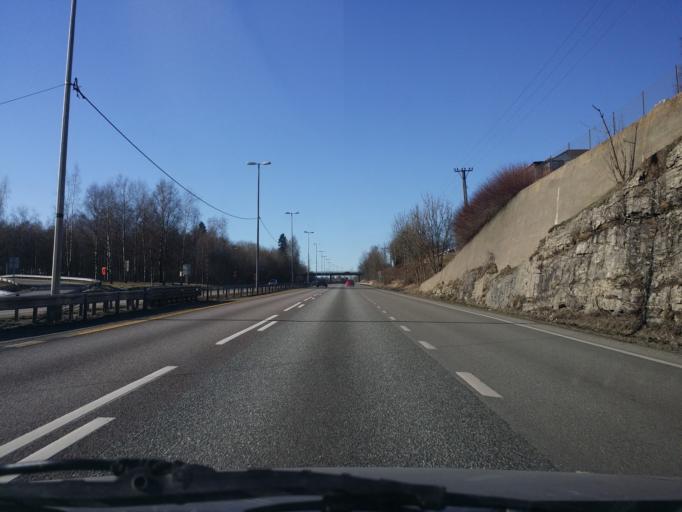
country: NO
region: Akershus
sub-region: Asker
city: Asker
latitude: 59.8308
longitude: 10.4121
